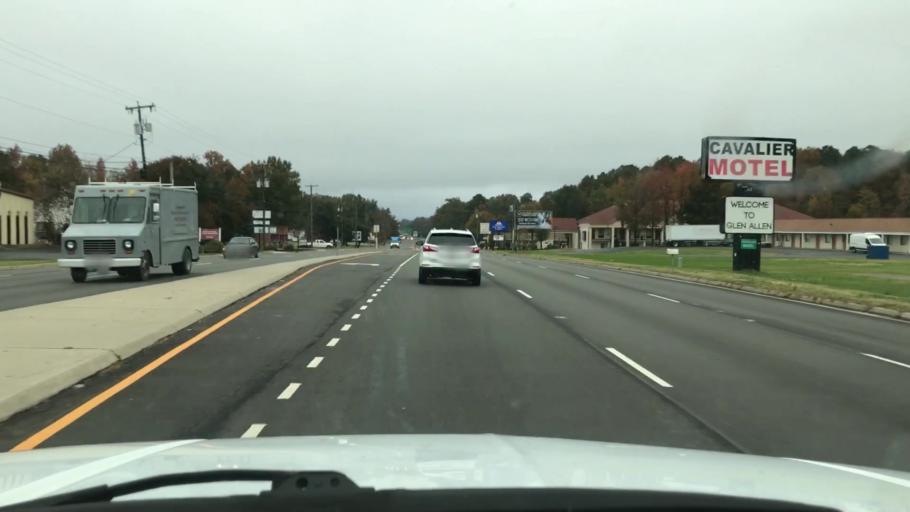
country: US
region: Virginia
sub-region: Henrico County
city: Chamberlayne
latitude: 37.6436
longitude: -77.4601
